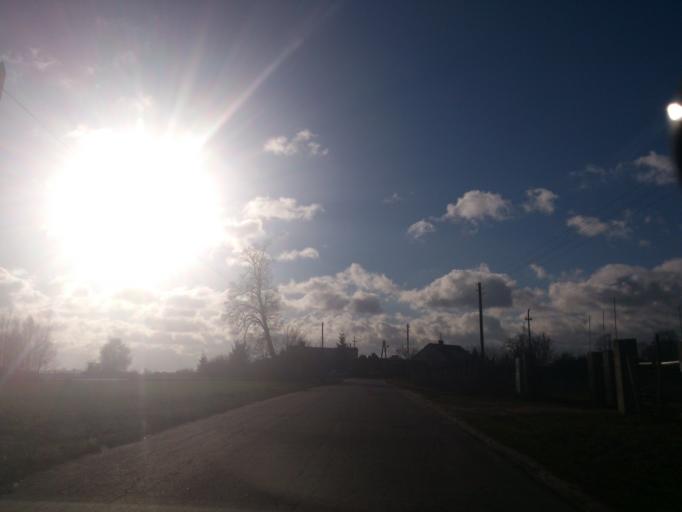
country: PL
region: Kujawsko-Pomorskie
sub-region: Powiat torunski
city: Lubicz Gorny
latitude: 53.0419
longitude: 18.8149
